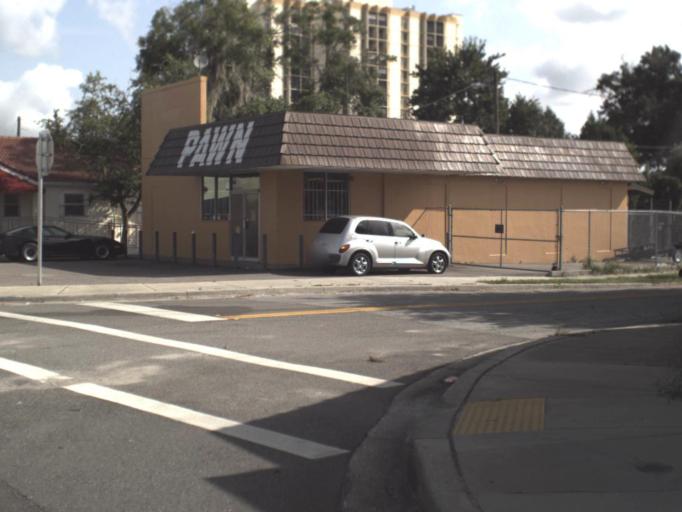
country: US
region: Florida
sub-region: Polk County
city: Winter Haven
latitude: 28.0314
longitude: -81.7329
